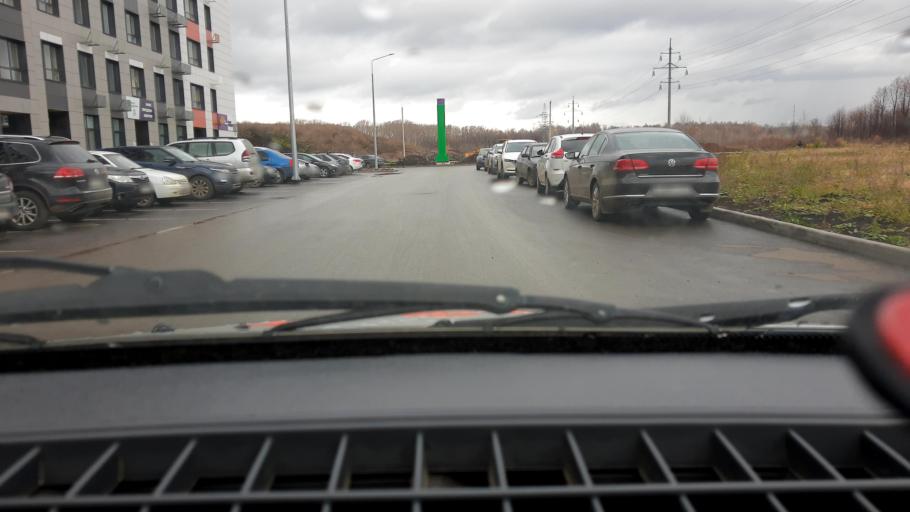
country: RU
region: Bashkortostan
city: Ufa
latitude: 54.6752
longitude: 55.9200
